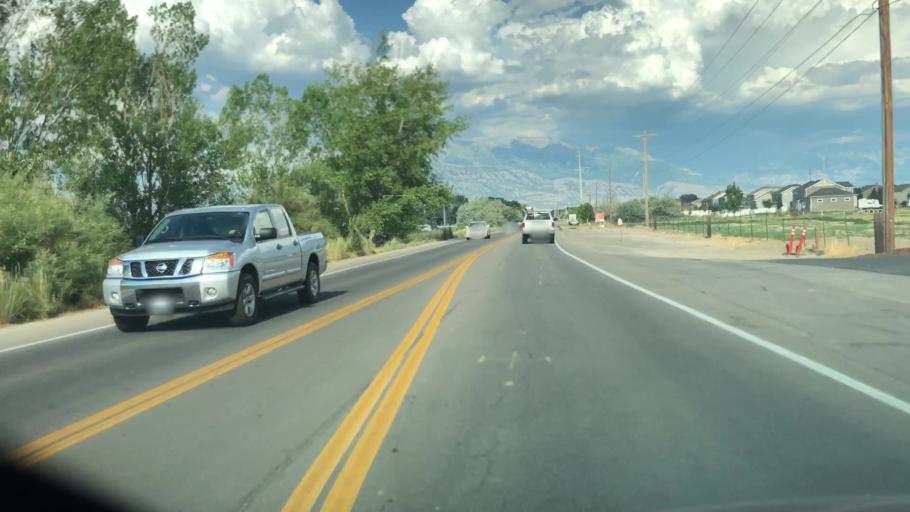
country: US
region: Utah
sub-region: Utah County
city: Saratoga Springs
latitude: 40.3875
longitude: -111.8988
